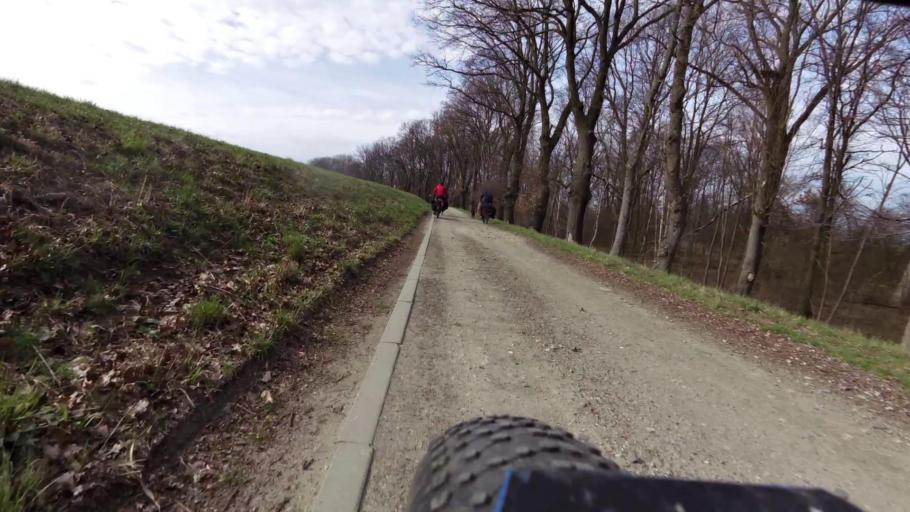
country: PL
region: Lubusz
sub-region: Powiat slubicki
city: Gorzyca
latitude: 52.5047
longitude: 14.6314
